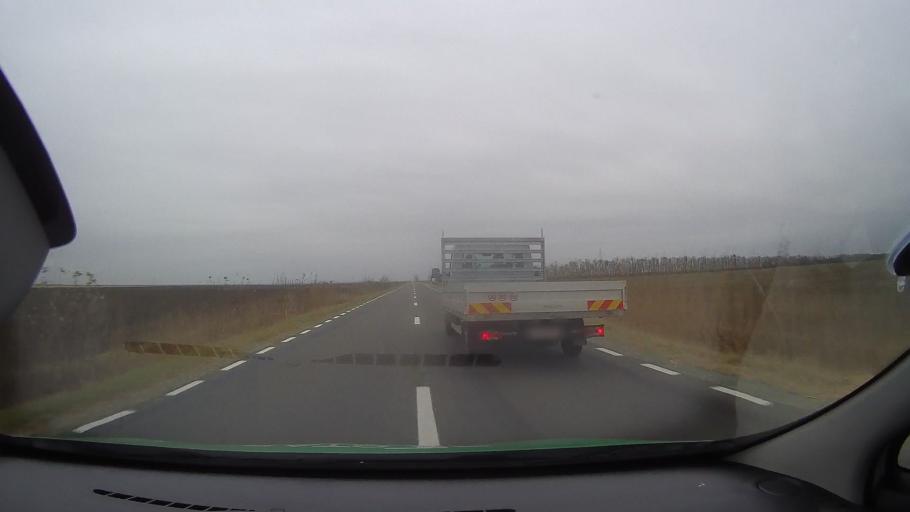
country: RO
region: Ialomita
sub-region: Comuna Gheorghe Lazar
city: Gheorghe Lazar
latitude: 44.6689
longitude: 27.4170
